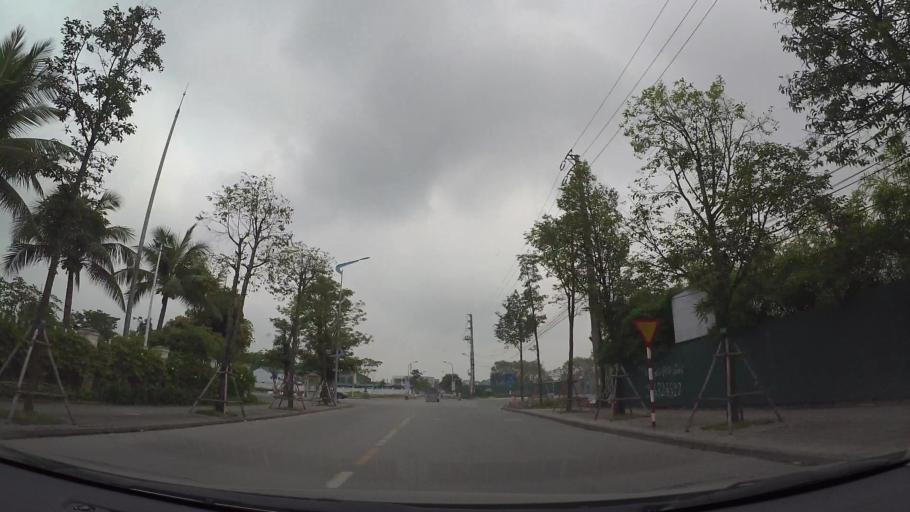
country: VN
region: Ha Noi
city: Trau Quy
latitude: 21.0397
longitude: 105.9236
